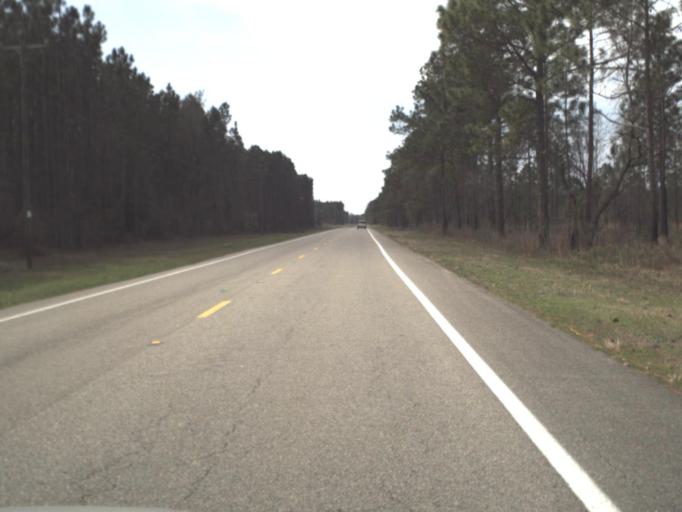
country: US
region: Florida
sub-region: Liberty County
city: Bristol
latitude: 30.4627
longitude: -84.9513
